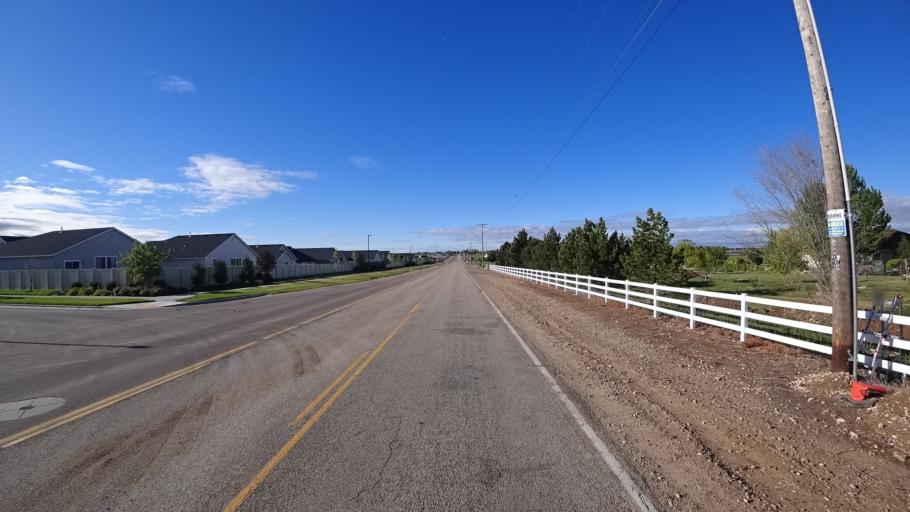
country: US
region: Idaho
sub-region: Ada County
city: Kuna
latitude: 43.5447
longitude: -116.4140
